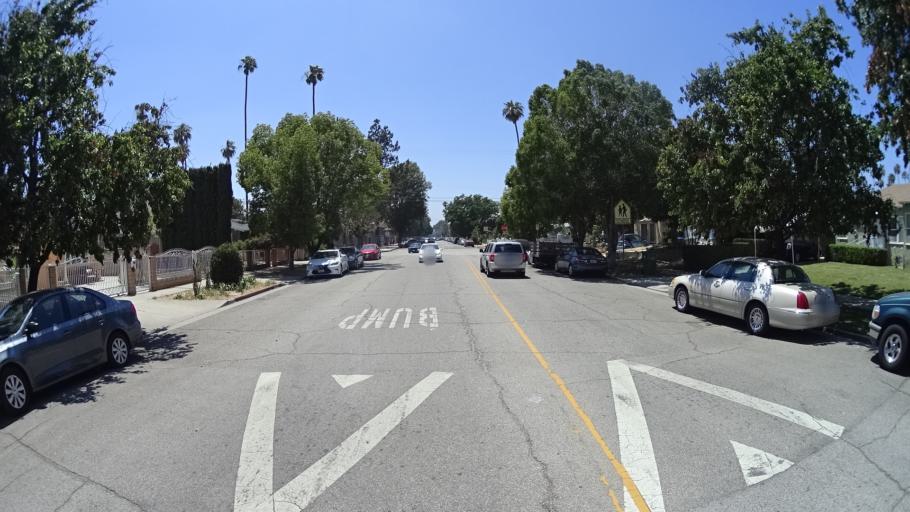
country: US
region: California
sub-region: Los Angeles County
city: Van Nuys
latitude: 34.1886
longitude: -118.4439
